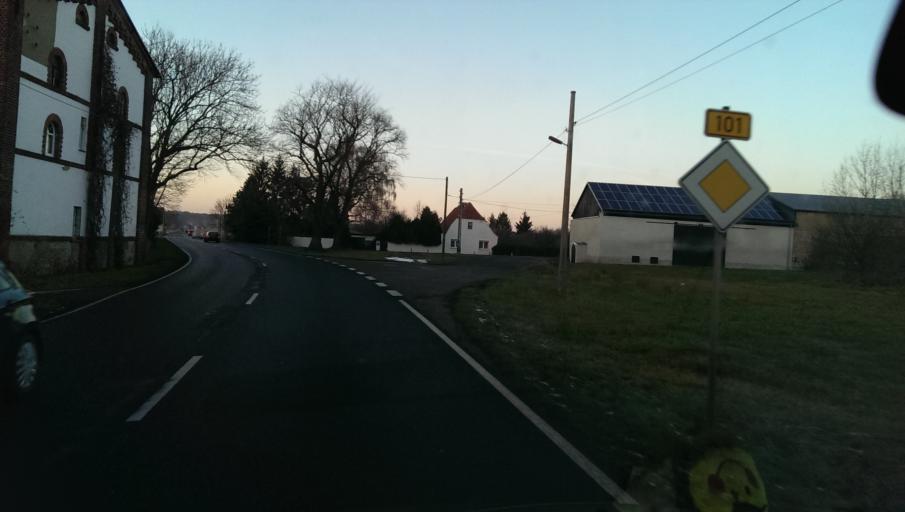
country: DE
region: Brandenburg
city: Schilda
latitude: 51.6325
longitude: 13.3174
